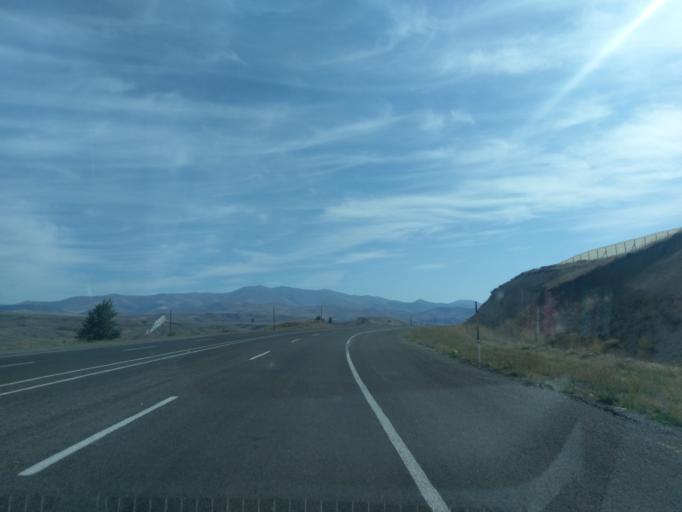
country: TR
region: Sivas
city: Imranli
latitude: 39.8712
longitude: 38.1831
